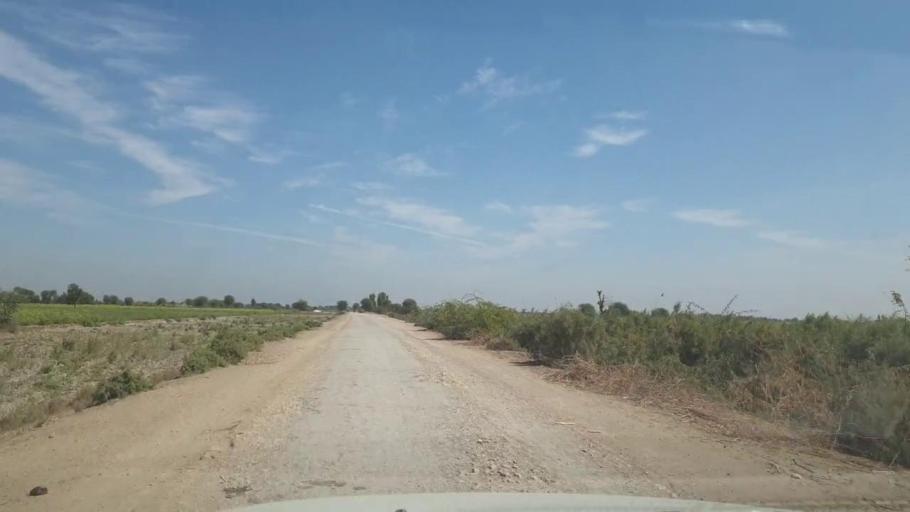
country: PK
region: Sindh
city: Mirpur Khas
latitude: 25.6059
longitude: 69.1888
